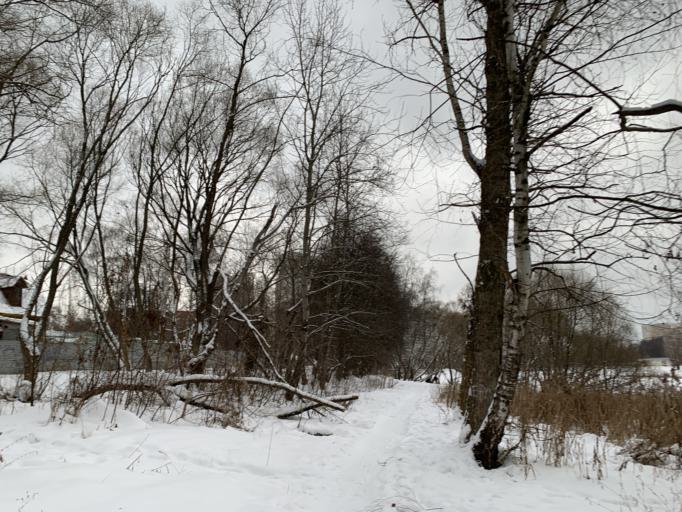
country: RU
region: Moskovskaya
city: Pushkino
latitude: 56.0069
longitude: 37.8610
